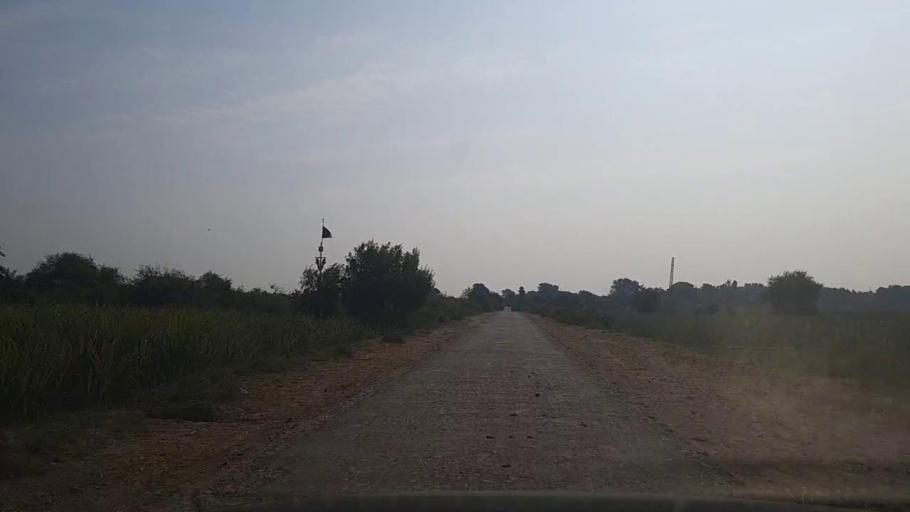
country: PK
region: Sindh
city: Bulri
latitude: 24.9710
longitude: 68.3285
